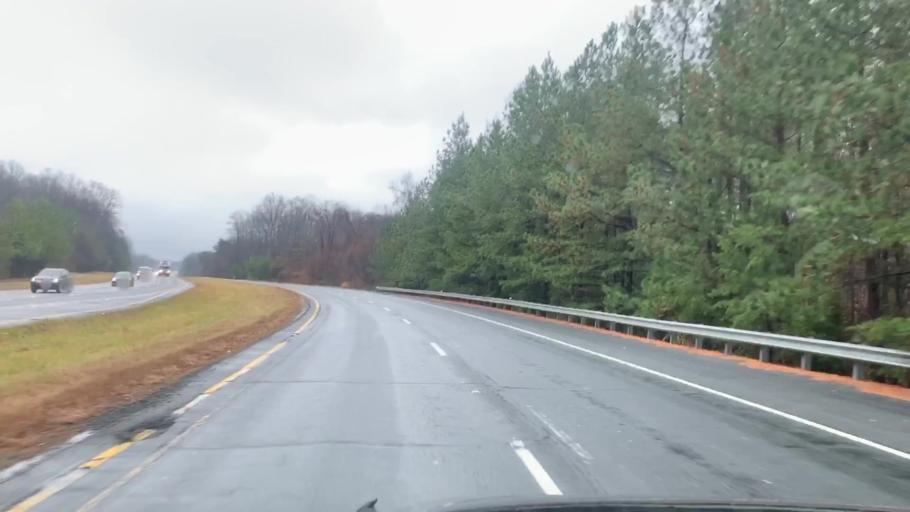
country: US
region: Virginia
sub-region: Fairfax County
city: Fairfax Station
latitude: 38.7773
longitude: -77.3263
